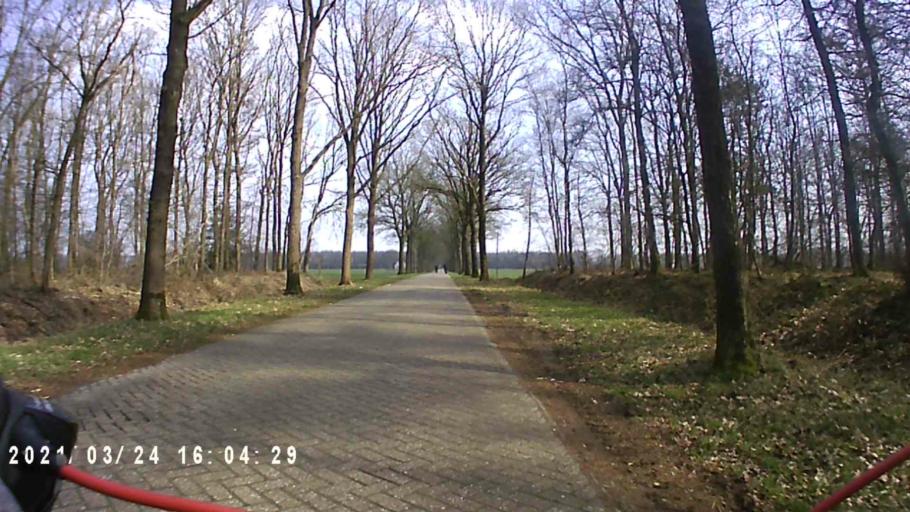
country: NL
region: Friesland
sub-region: Gemeente Heerenveen
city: Jubbega
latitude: 53.0319
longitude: 6.2095
